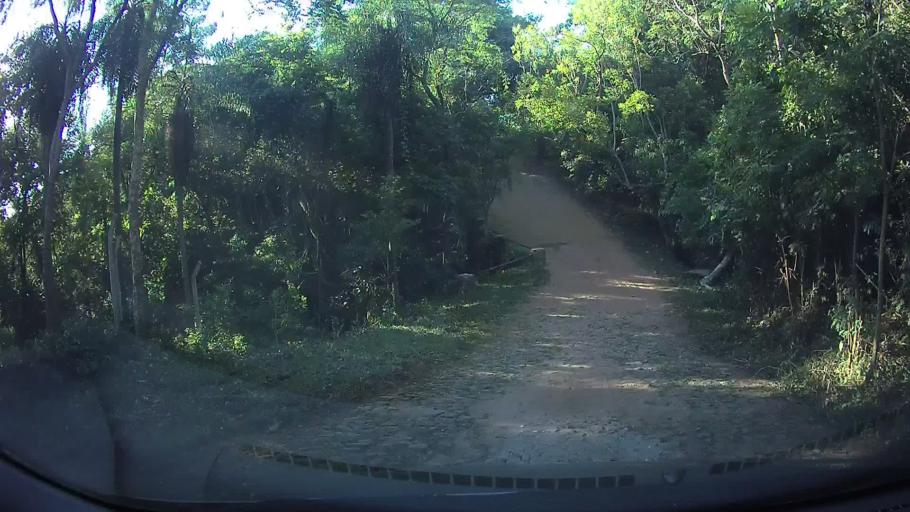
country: PY
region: Cordillera
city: San Bernardino
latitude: -25.3087
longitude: -57.2677
